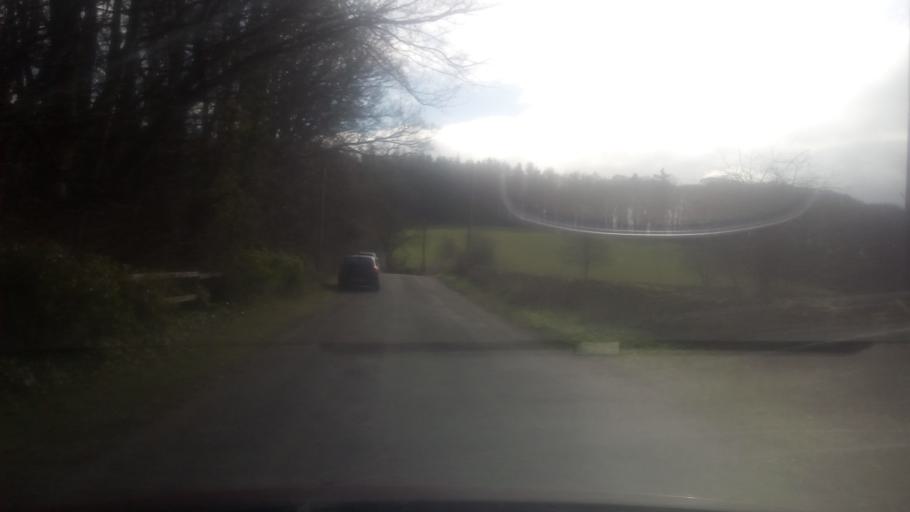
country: GB
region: Scotland
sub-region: The Scottish Borders
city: Jedburgh
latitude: 55.5046
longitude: -2.5728
